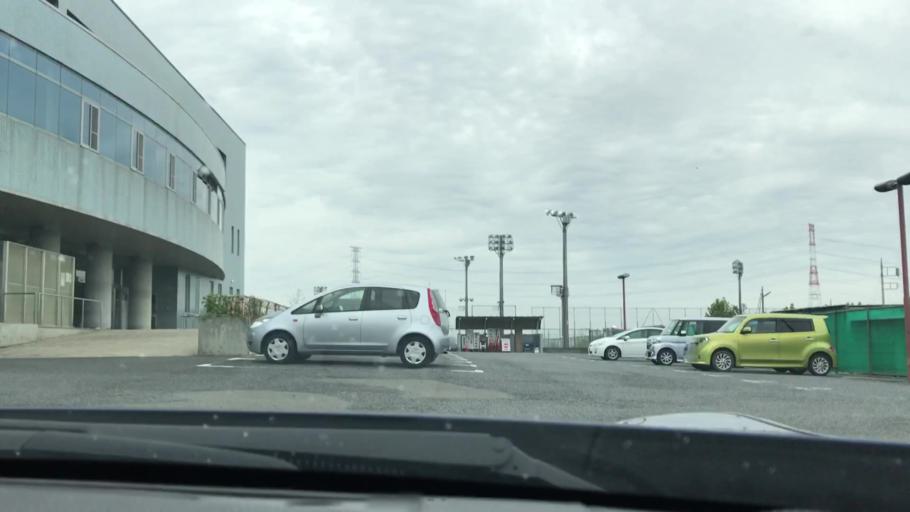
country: JP
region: Gunma
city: Kanekomachi
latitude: 36.3888
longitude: 138.9648
